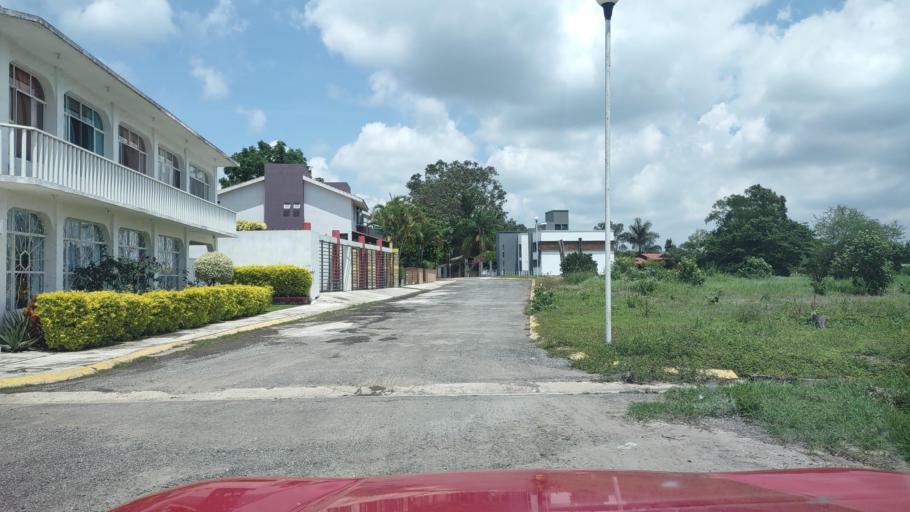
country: MX
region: Veracruz
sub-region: Emiliano Zapata
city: Dos Rios
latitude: 19.4646
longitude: -96.7896
